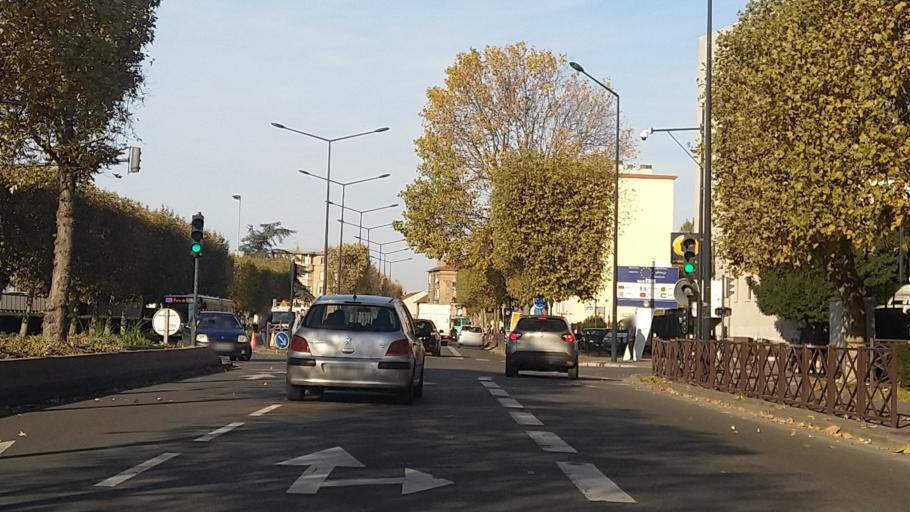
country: FR
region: Ile-de-France
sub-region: Departement de Seine-Saint-Denis
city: Stains
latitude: 48.9472
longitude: 2.3865
